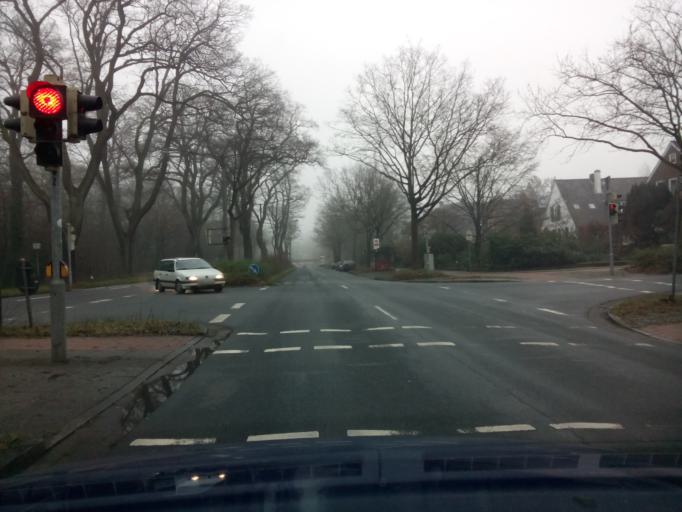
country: DE
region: Bremen
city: Bremen
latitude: 53.0990
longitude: 8.8367
